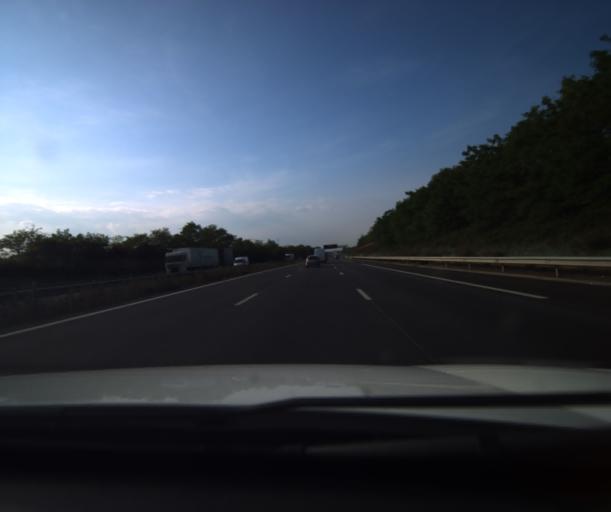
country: FR
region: Midi-Pyrenees
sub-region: Departement de la Haute-Garonne
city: Saint-Alban
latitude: 43.6954
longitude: 1.4091
